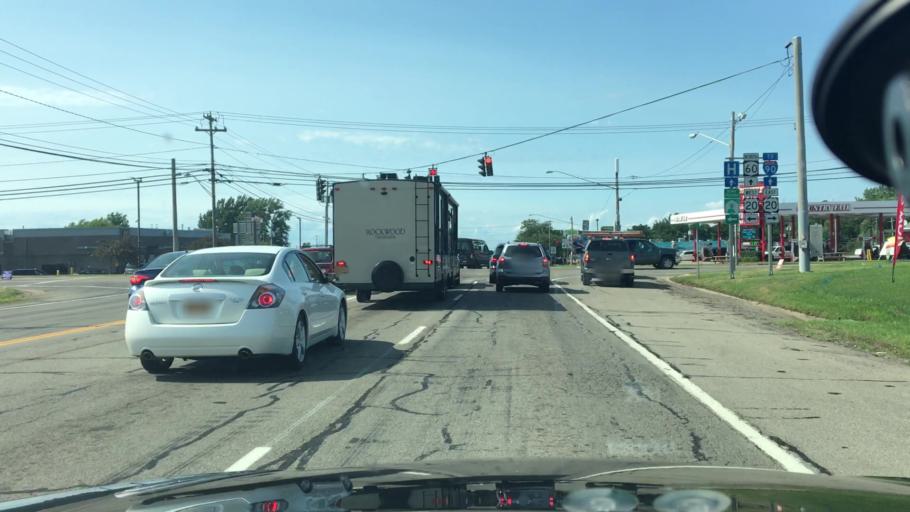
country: US
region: New York
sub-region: Chautauqua County
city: Fredonia
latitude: 42.4501
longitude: -79.3077
